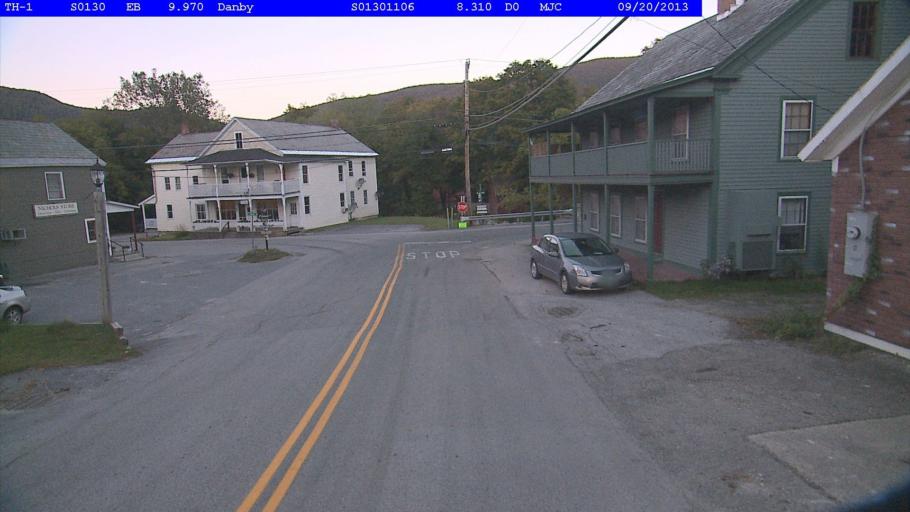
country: US
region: Vermont
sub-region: Bennington County
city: Manchester Center
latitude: 43.3466
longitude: -72.9968
